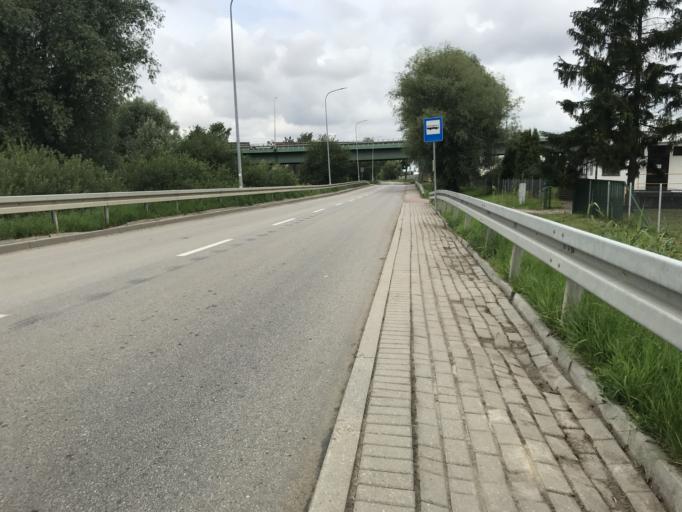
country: PL
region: Warmian-Masurian Voivodeship
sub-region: Powiat elblaski
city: Elblag
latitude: 54.1711
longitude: 19.3867
